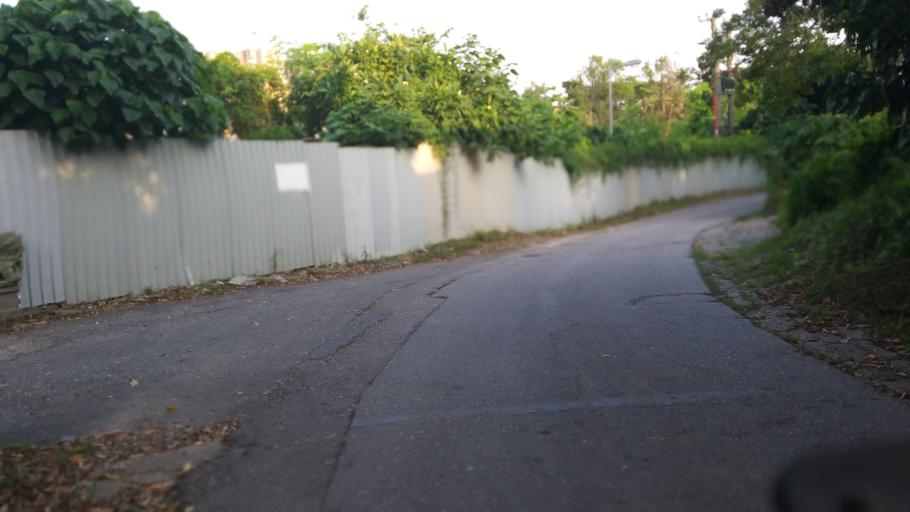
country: HK
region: Yuen Long
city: Yuen Long Kau Hui
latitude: 22.4482
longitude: 114.0147
